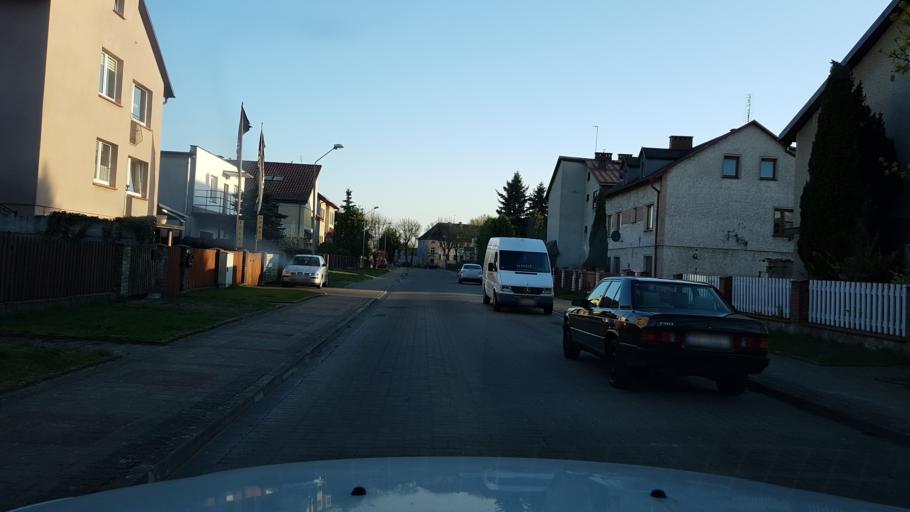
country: PL
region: West Pomeranian Voivodeship
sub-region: Powiat bialogardzki
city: Bialogard
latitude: 54.0091
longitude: 16.0040
